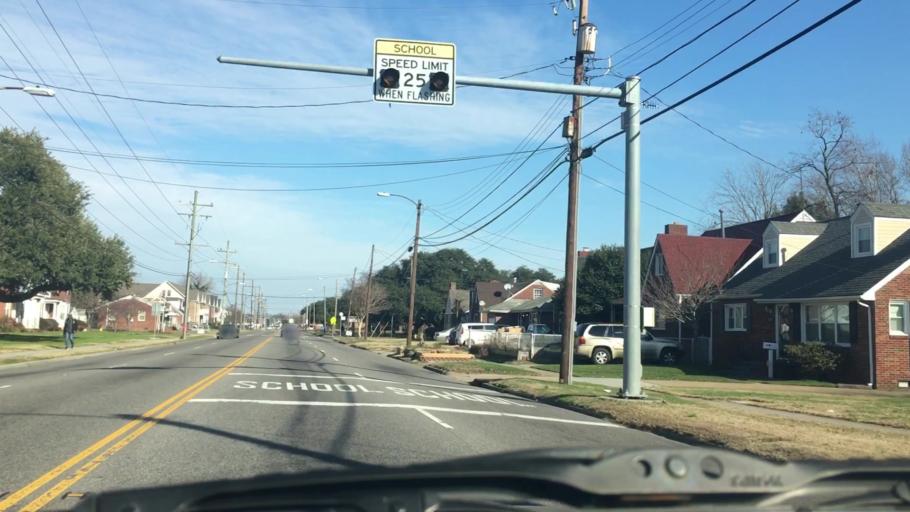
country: US
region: Virginia
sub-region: City of Norfolk
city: Norfolk
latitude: 36.8568
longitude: -76.2546
